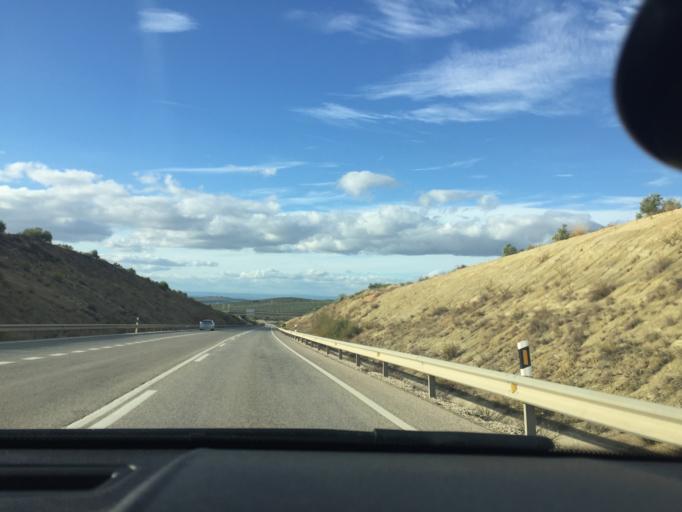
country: ES
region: Andalusia
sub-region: Provincia de Jaen
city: Torredonjimeno
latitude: 37.7599
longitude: -3.9652
